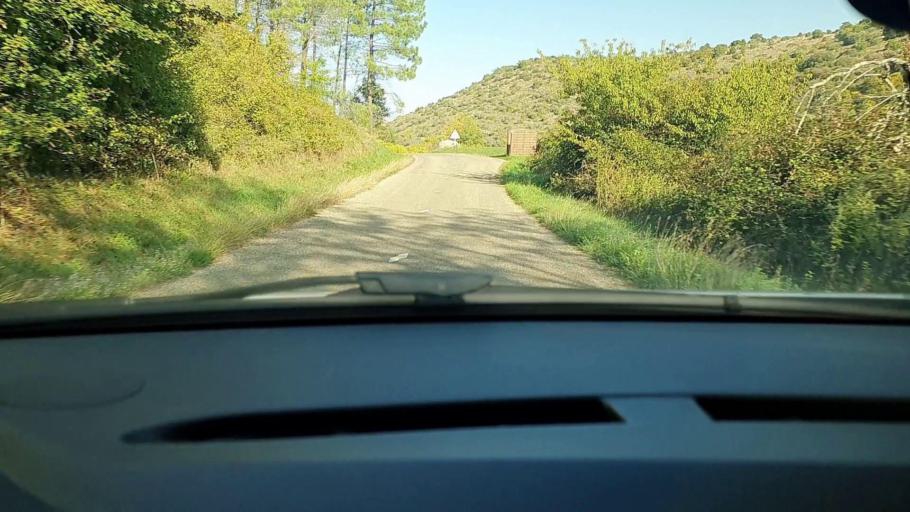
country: FR
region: Languedoc-Roussillon
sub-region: Departement du Gard
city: Molieres-sur-Ceze
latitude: 44.3071
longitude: 4.1462
